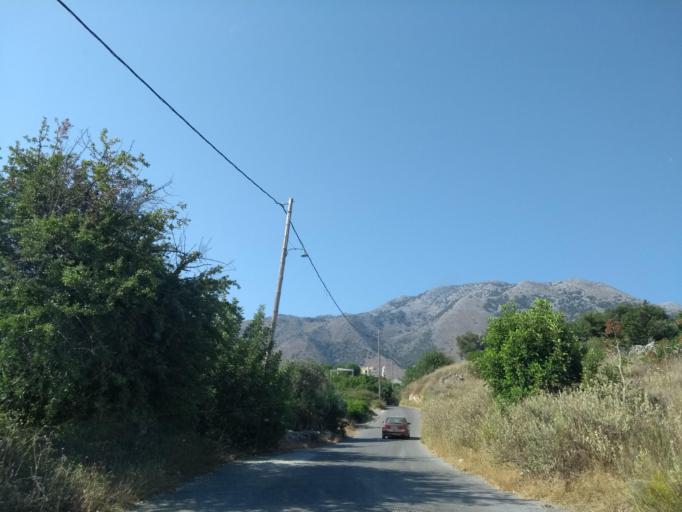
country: GR
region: Crete
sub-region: Nomos Chanias
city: Georgioupolis
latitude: 35.3185
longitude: 24.2965
